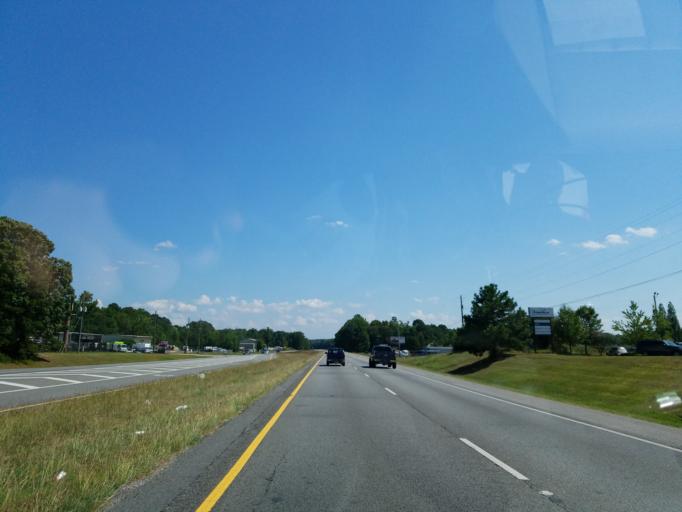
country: US
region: Georgia
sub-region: Spalding County
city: Griffin
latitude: 33.2170
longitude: -84.2889
